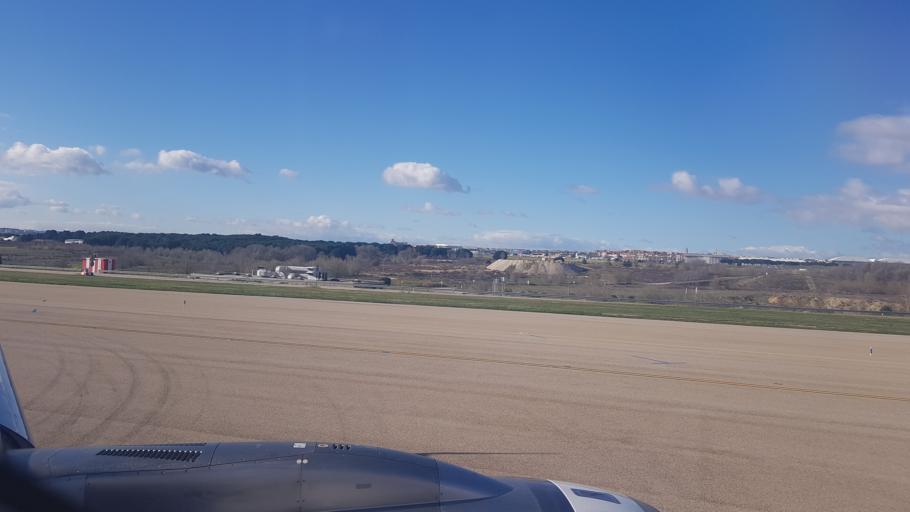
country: ES
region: Madrid
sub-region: Provincia de Madrid
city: Barajas de Madrid
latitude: 40.4887
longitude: -3.5540
